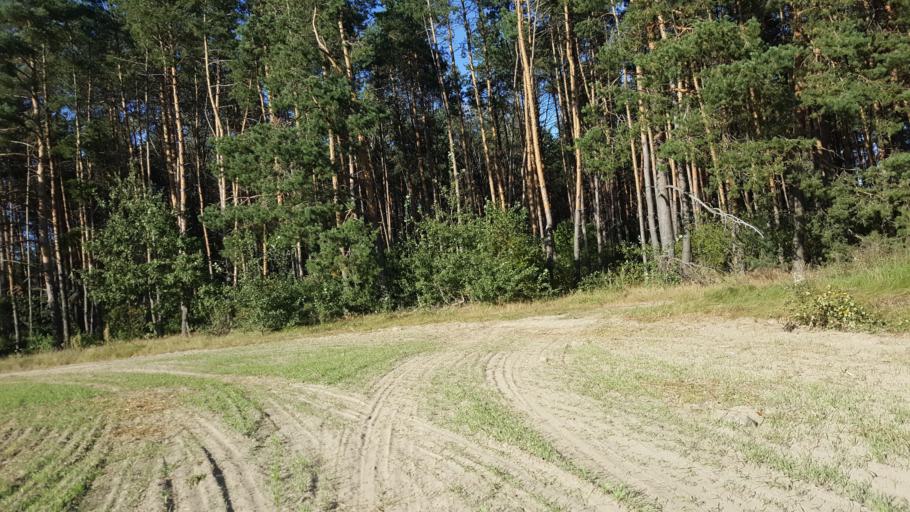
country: PL
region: Lublin Voivodeship
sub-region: Powiat bialski
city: Janow Podlaski
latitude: 52.3036
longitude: 23.2481
